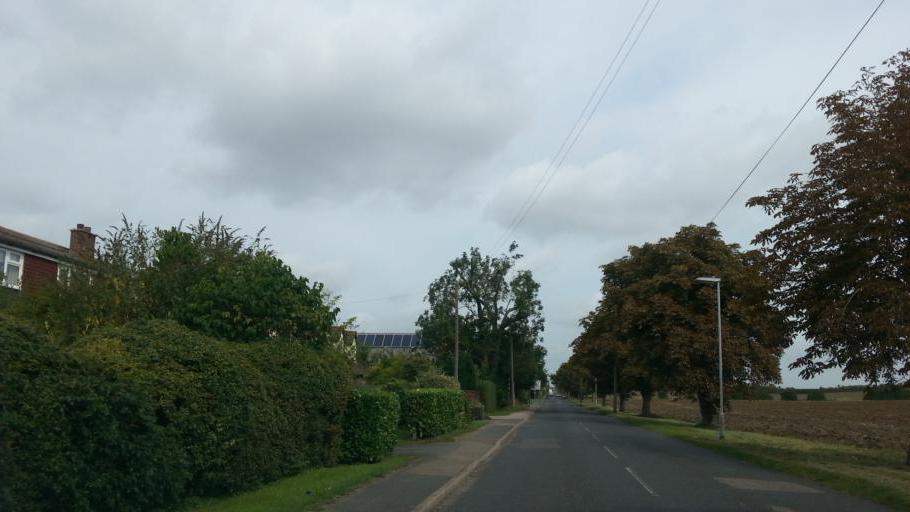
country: GB
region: England
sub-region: Cambridgeshire
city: Comberton
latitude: 52.1892
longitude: 0.0297
